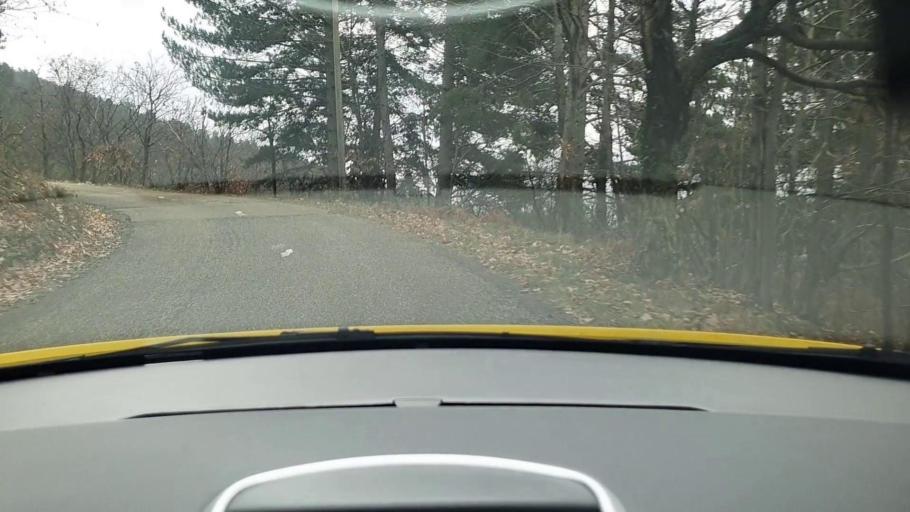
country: FR
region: Languedoc-Roussillon
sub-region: Departement du Gard
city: Besseges
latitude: 44.3627
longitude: 4.0233
